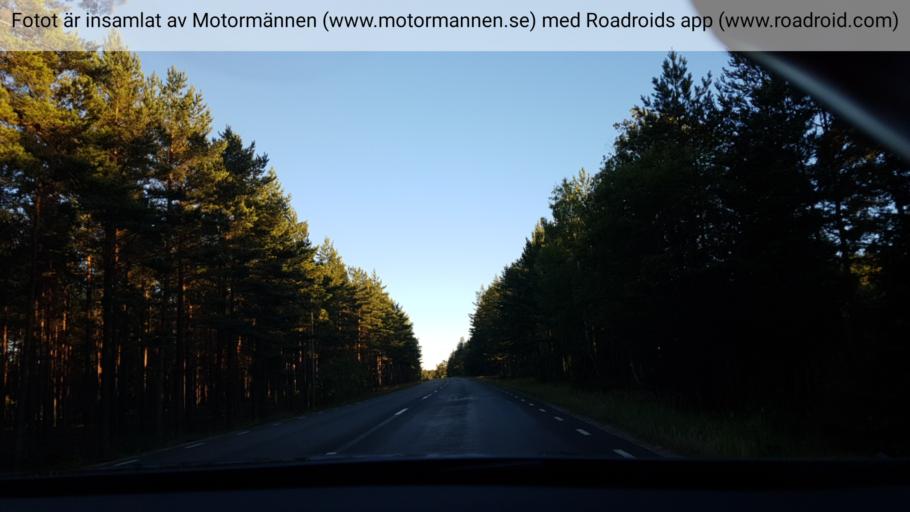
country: SE
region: Vaestra Goetaland
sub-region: Karlsborgs Kommun
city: Molltorp
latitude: 58.4788
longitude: 14.4084
